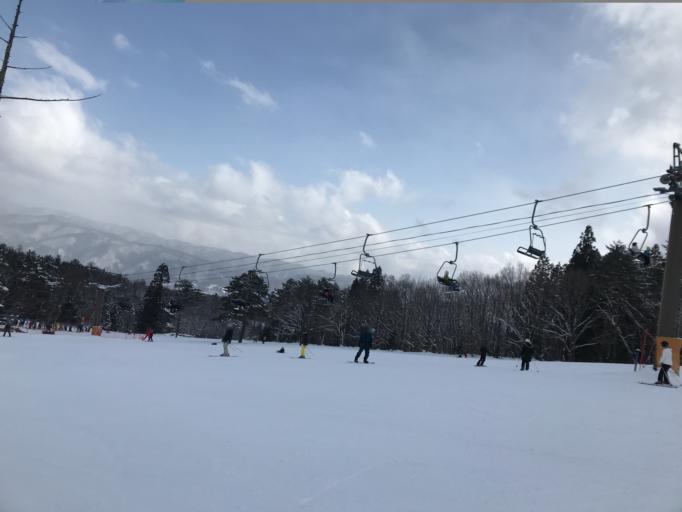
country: JP
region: Nagano
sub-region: Kitaazumi Gun
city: Hakuba
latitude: 36.7101
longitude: 137.8300
